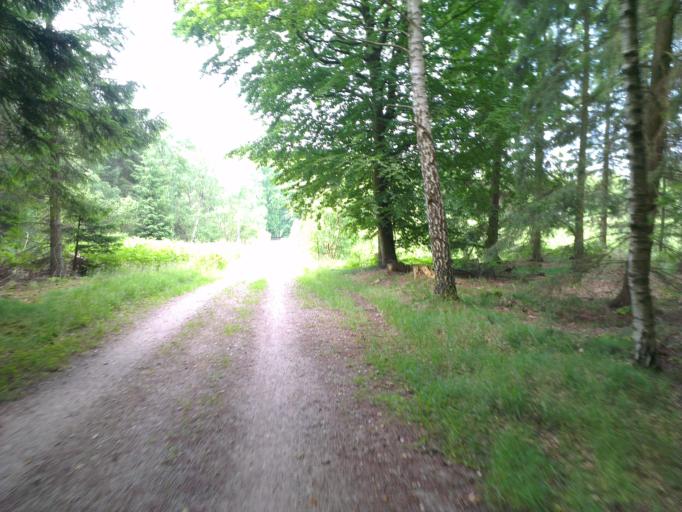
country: DK
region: Capital Region
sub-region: Allerod Kommune
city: Lillerod
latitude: 55.9106
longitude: 12.3528
